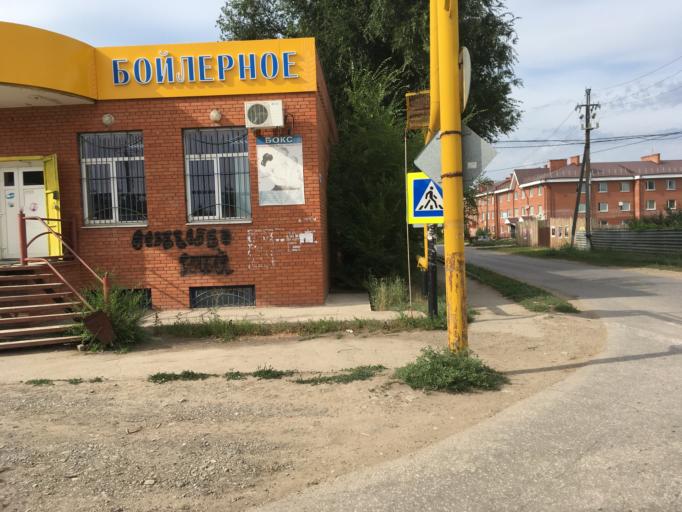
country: RU
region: Samara
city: Bezenchuk
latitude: 52.9884
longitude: 49.4412
